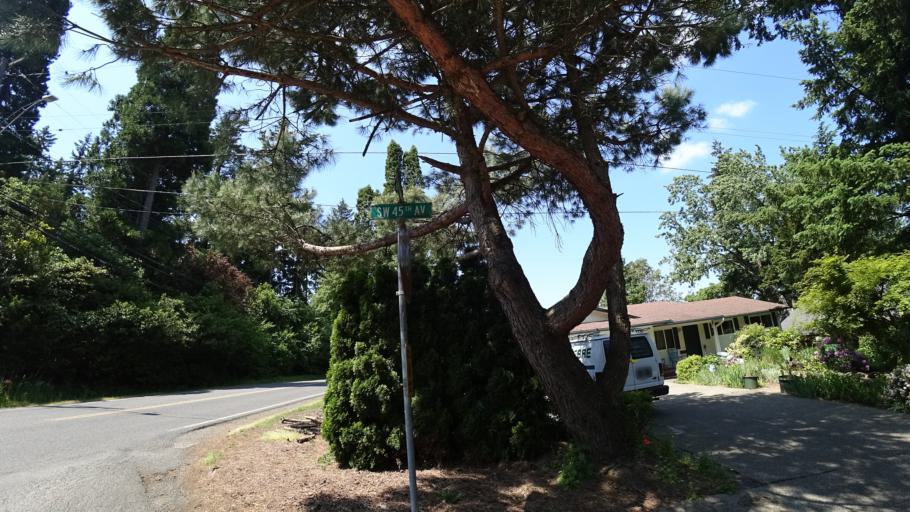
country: US
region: Oregon
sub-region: Washington County
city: Metzger
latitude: 45.4455
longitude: -122.7231
